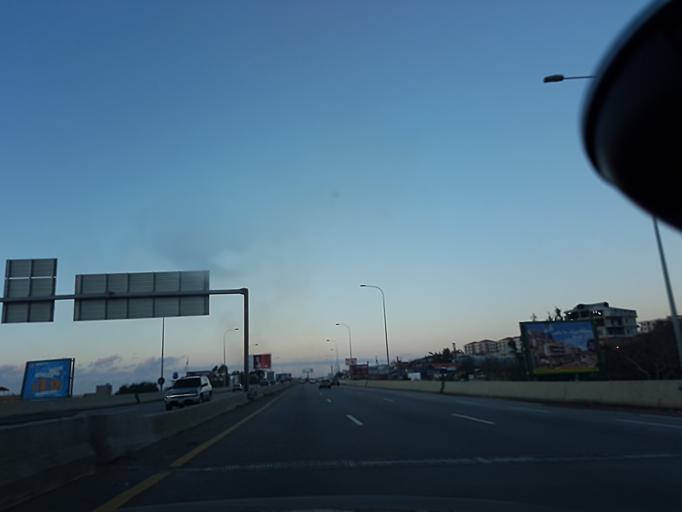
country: LB
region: Liban-Sud
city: Sidon
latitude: 33.6266
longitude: 35.4021
